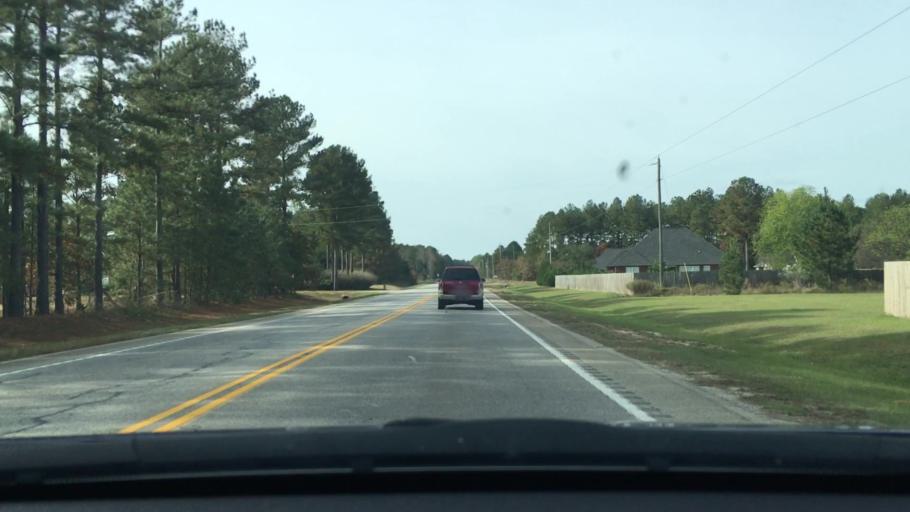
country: US
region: South Carolina
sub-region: Sumter County
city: Cherryvale
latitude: 33.9393
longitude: -80.4778
